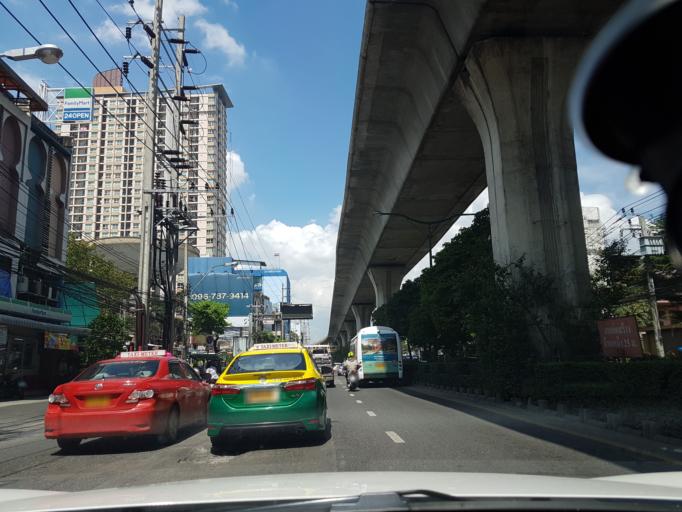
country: TH
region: Bangkok
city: Phra Khanong
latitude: 13.7069
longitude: 100.6001
